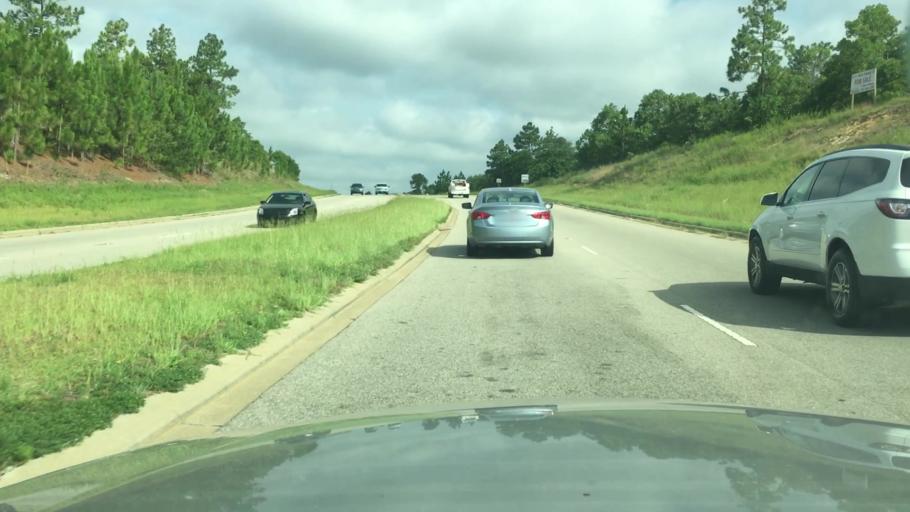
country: US
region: North Carolina
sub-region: Cumberland County
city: Hope Mills
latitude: 34.9879
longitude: -78.9353
